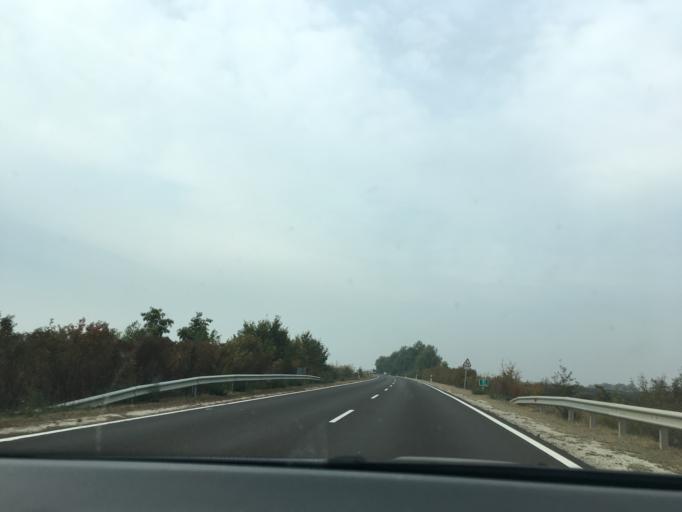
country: HU
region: Jasz-Nagykun-Szolnok
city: Zagyvarekas
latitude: 47.1886
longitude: 20.0939
